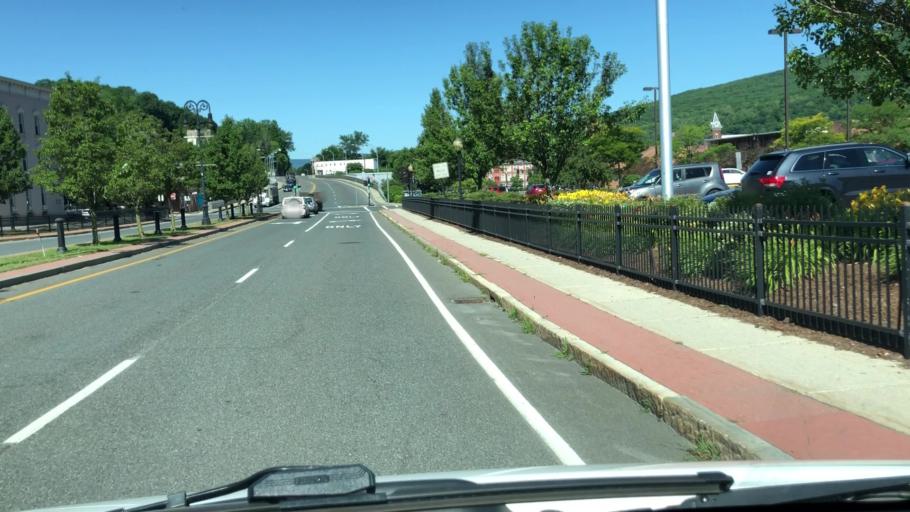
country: US
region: Massachusetts
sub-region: Berkshire County
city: North Adams
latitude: 42.7003
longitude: -73.1106
